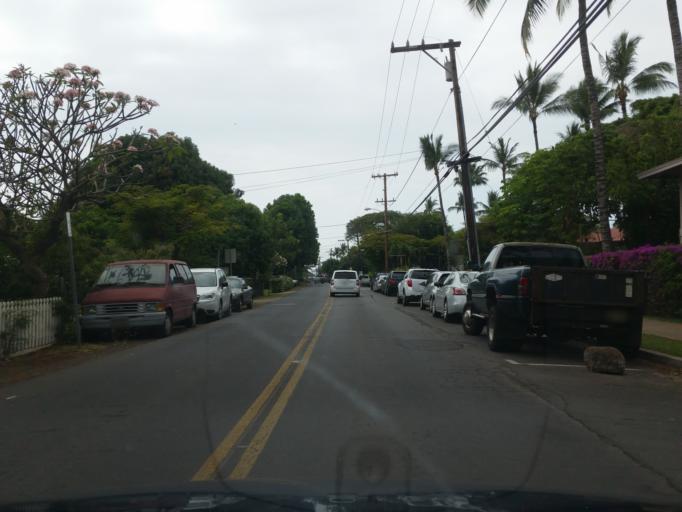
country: US
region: Hawaii
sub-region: Maui County
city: Lahaina
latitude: 20.8730
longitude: -156.6752
